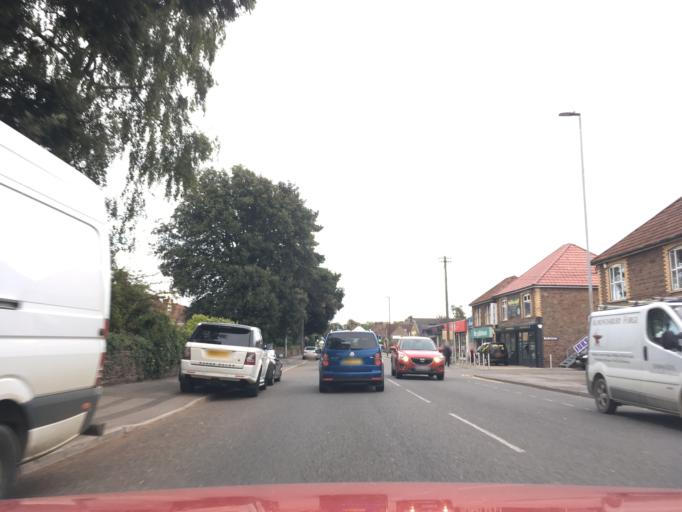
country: GB
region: England
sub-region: South Gloucestershire
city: Yate
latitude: 51.5407
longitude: -2.4243
